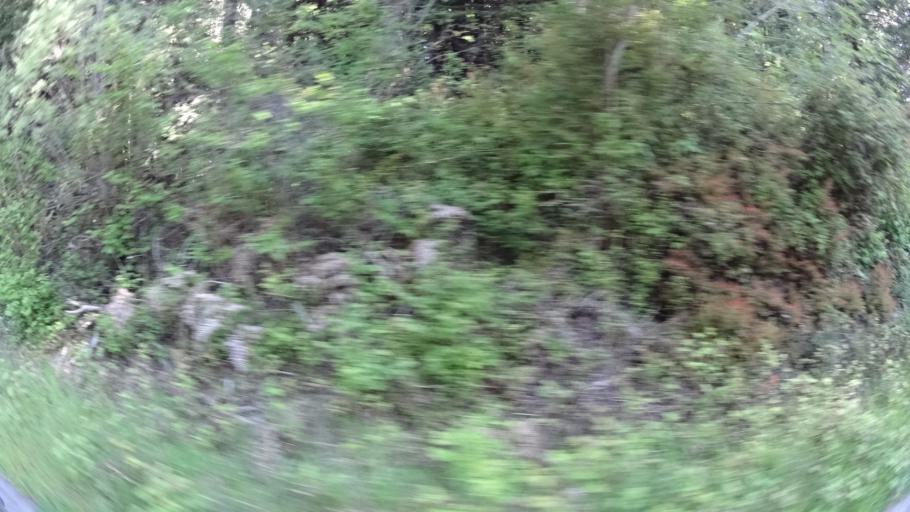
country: US
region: California
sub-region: Humboldt County
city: Rio Dell
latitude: 40.4372
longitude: -123.9668
